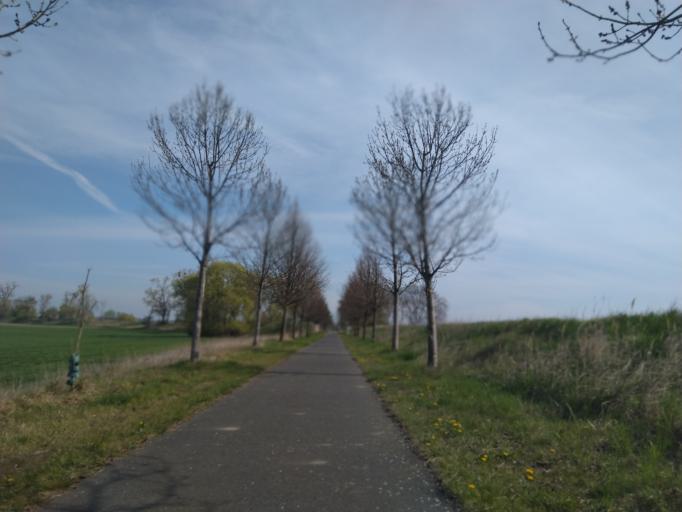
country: DE
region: Brandenburg
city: Wriezen
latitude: 52.7346
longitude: 14.1538
